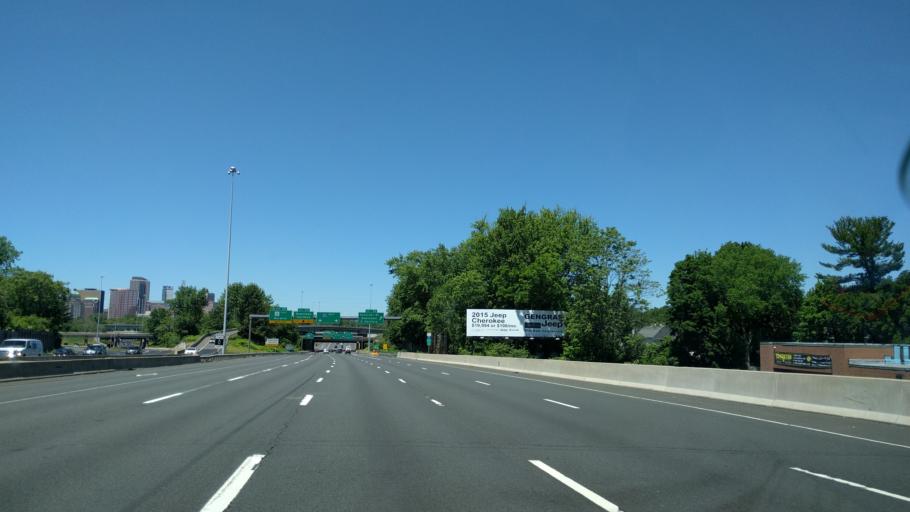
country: US
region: Connecticut
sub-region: Hartford County
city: Hartford
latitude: 41.7650
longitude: -72.6470
